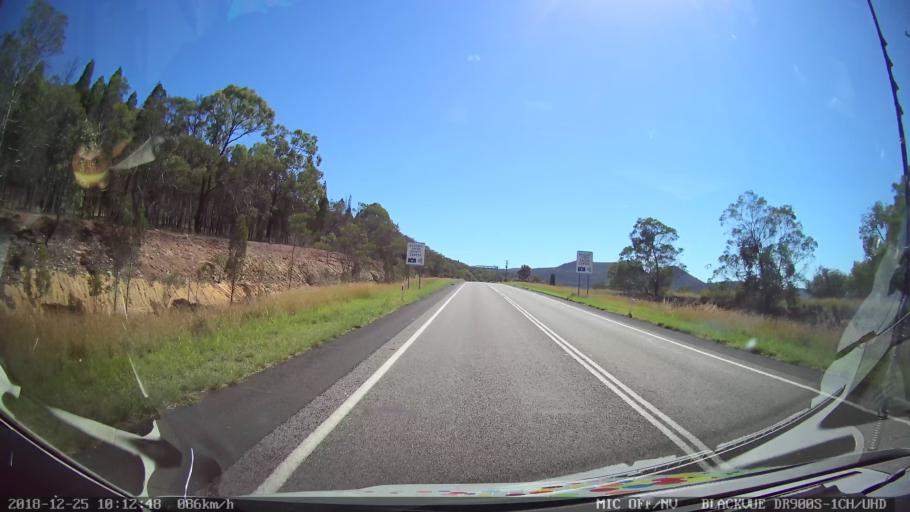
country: AU
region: New South Wales
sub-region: Muswellbrook
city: Denman
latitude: -32.3281
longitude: 150.5359
